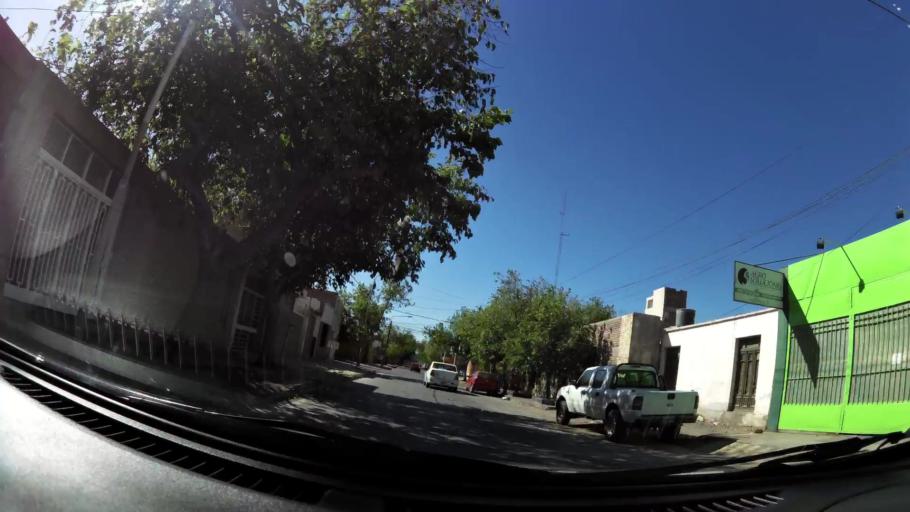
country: AR
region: San Juan
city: San Juan
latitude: -31.5450
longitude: -68.5341
